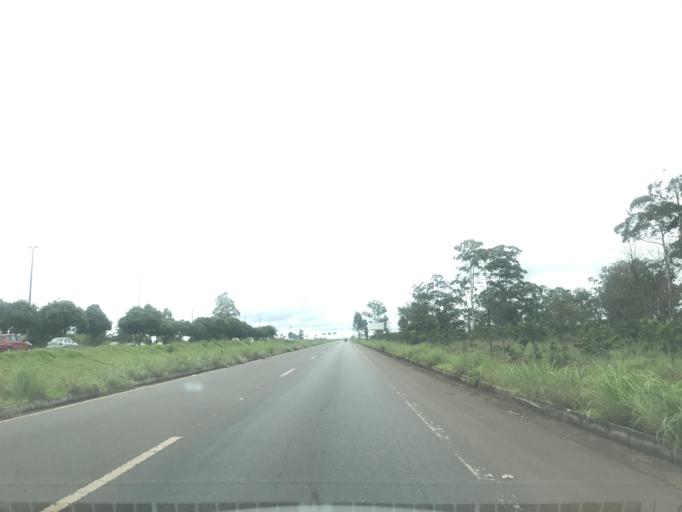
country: BR
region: Federal District
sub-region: Brasilia
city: Brasilia
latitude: -15.6852
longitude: -47.8496
